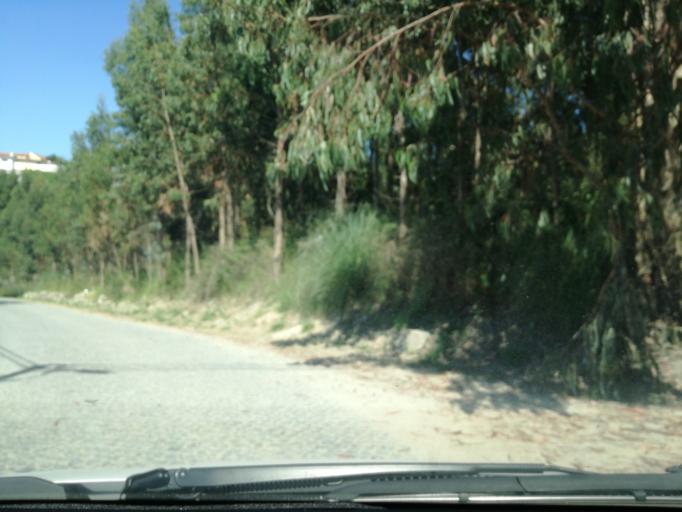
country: PT
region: Porto
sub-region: Maia
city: Nogueira
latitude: 41.2486
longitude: -8.6006
